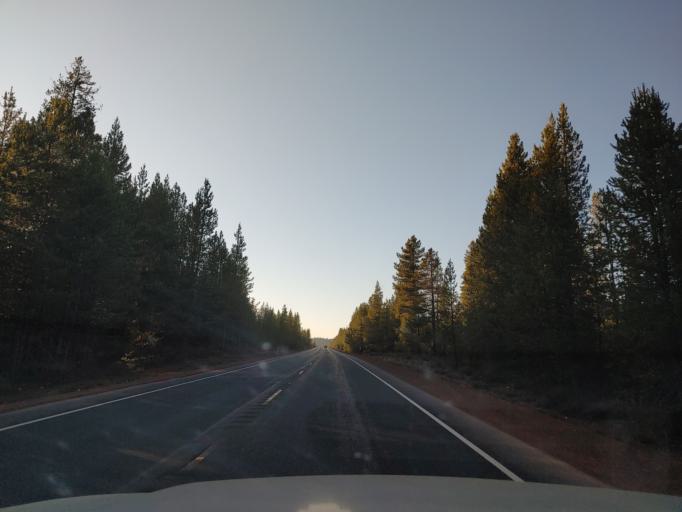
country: US
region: Oregon
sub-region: Deschutes County
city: La Pine
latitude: 43.4211
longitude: -121.8417
